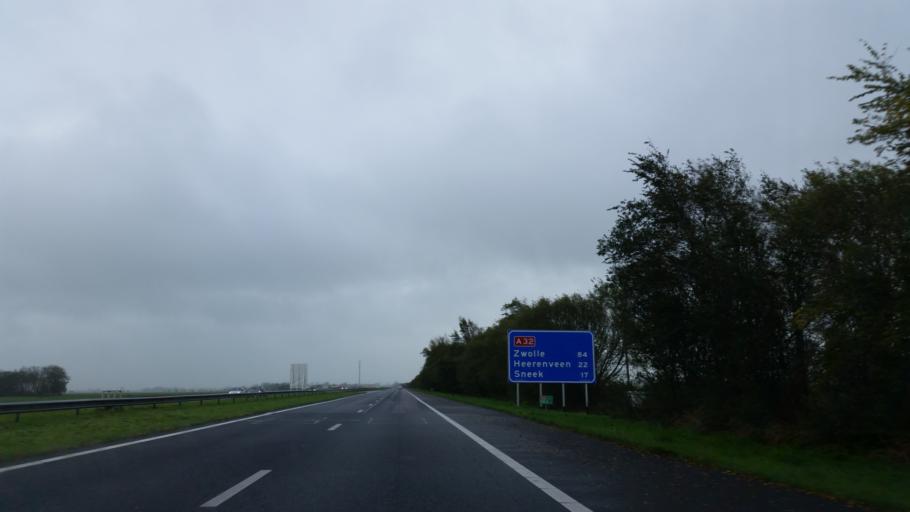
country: NL
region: Friesland
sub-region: Gemeente Leeuwarden
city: Wirdum
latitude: 53.1379
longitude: 5.7991
